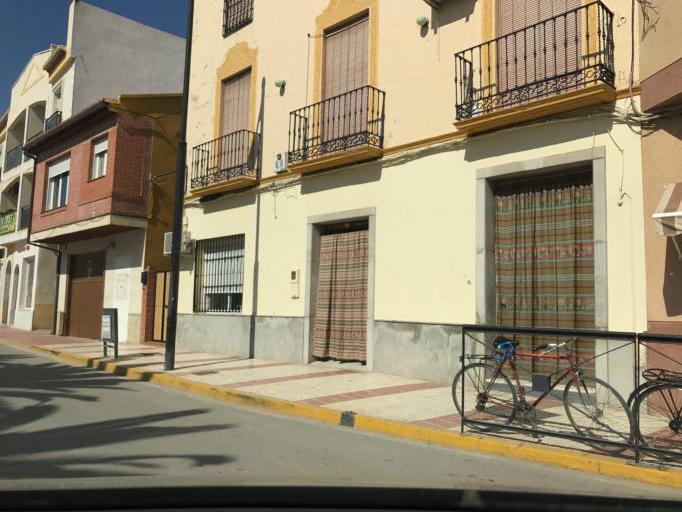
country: ES
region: Andalusia
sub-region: Provincia de Granada
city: Chauchina
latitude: 37.2015
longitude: -3.7720
